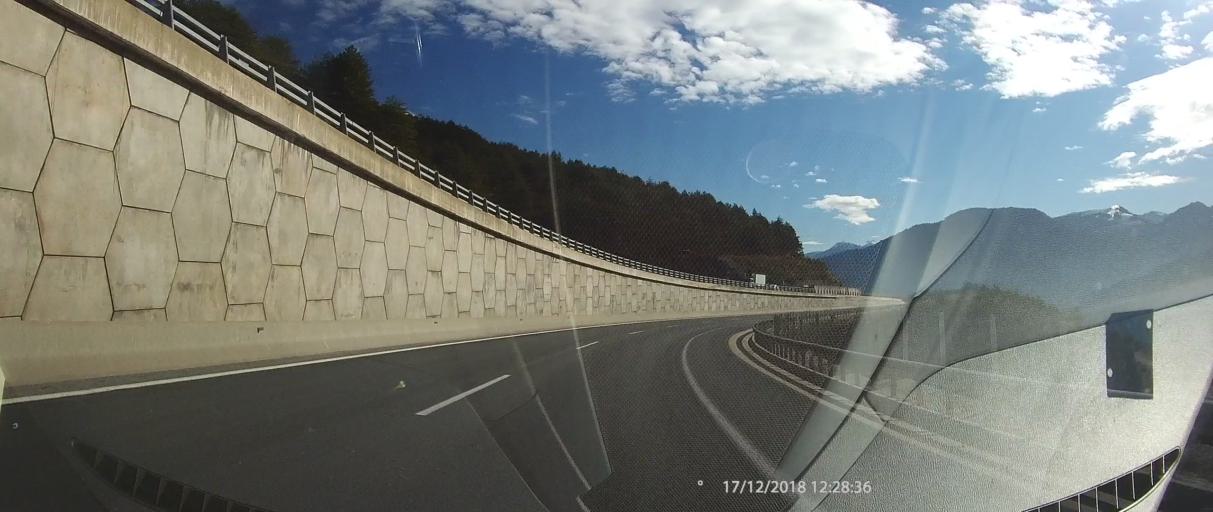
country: GR
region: Epirus
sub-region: Nomos Ioanninon
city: Metsovo
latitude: 39.7903
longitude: 21.2787
